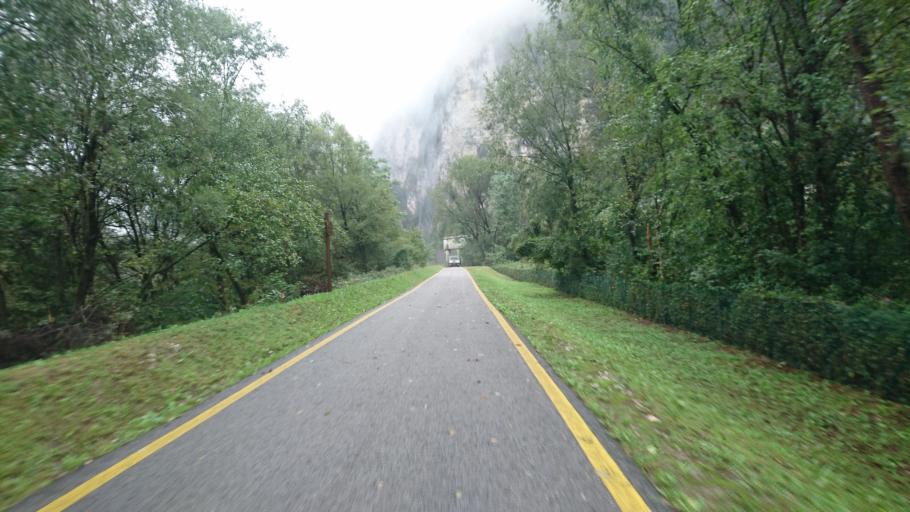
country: IT
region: Trentino-Alto Adige
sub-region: Provincia di Trento
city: Grigno
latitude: 46.0168
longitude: 11.6098
